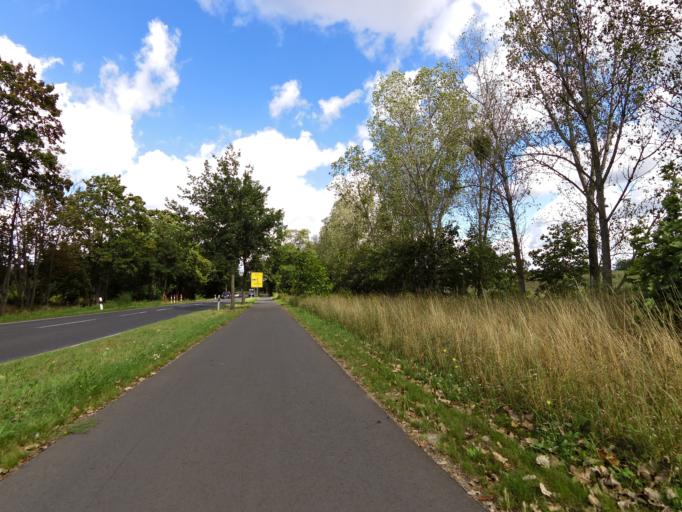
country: DE
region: Brandenburg
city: Grossbeeren
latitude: 52.3715
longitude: 13.3189
